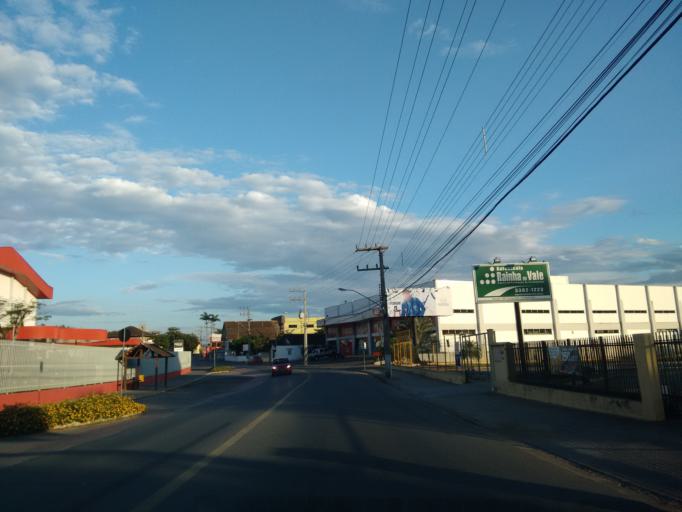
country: BR
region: Santa Catarina
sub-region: Timbo
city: Timbo
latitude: -26.8305
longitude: -49.2741
